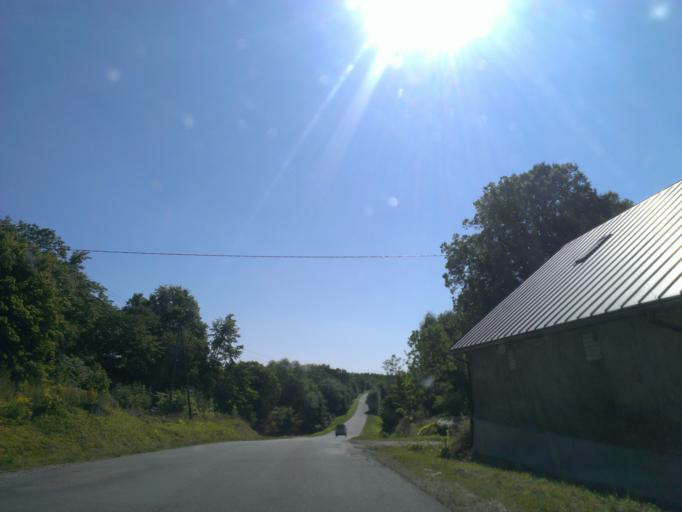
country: LV
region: Sigulda
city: Sigulda
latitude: 57.1320
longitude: 24.8377
